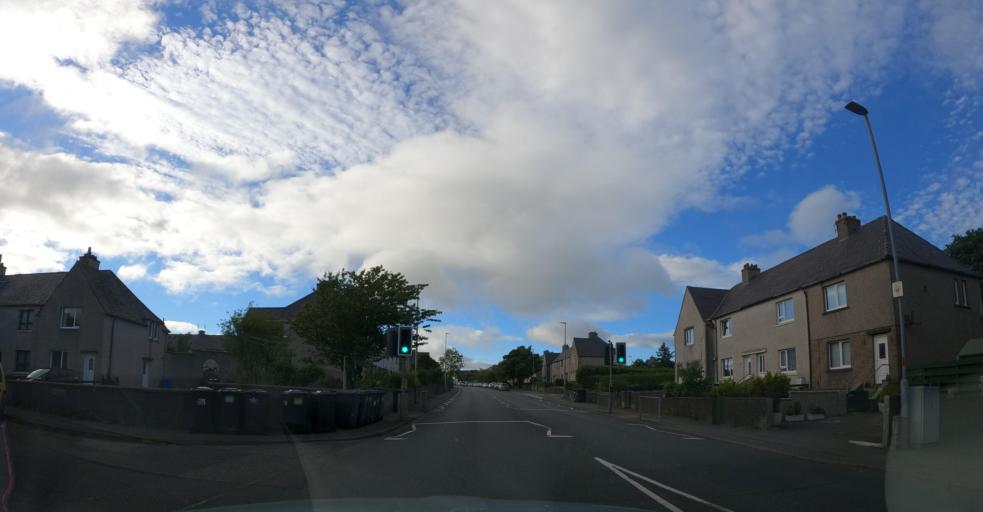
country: GB
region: Scotland
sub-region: Eilean Siar
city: Isle of Lewis
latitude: 58.2175
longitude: -6.3859
